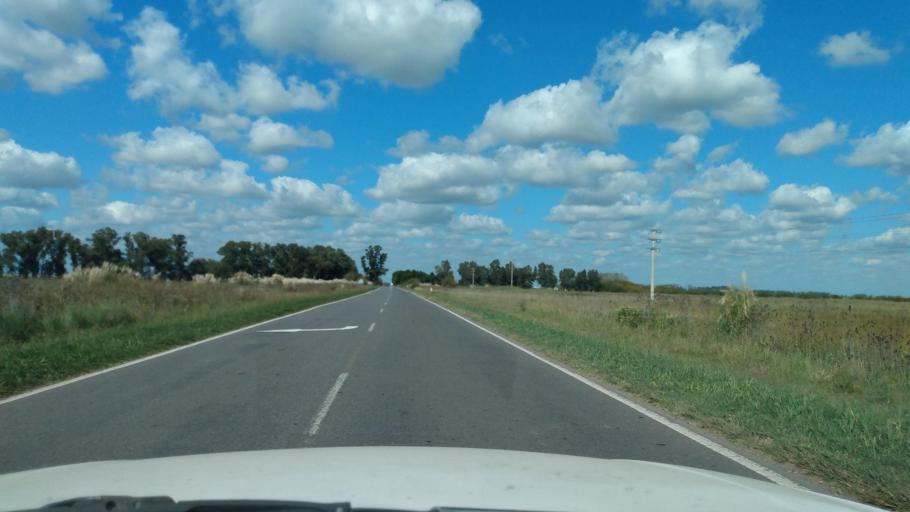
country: AR
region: Buenos Aires
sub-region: Partido de Navarro
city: Navarro
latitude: -34.8823
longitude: -59.3405
